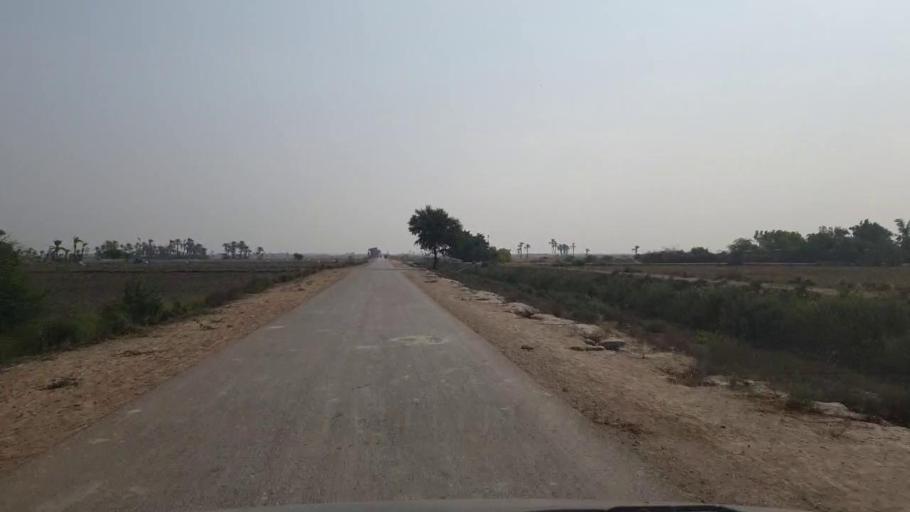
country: PK
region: Sindh
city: Tando Muhammad Khan
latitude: 25.1052
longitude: 68.3694
